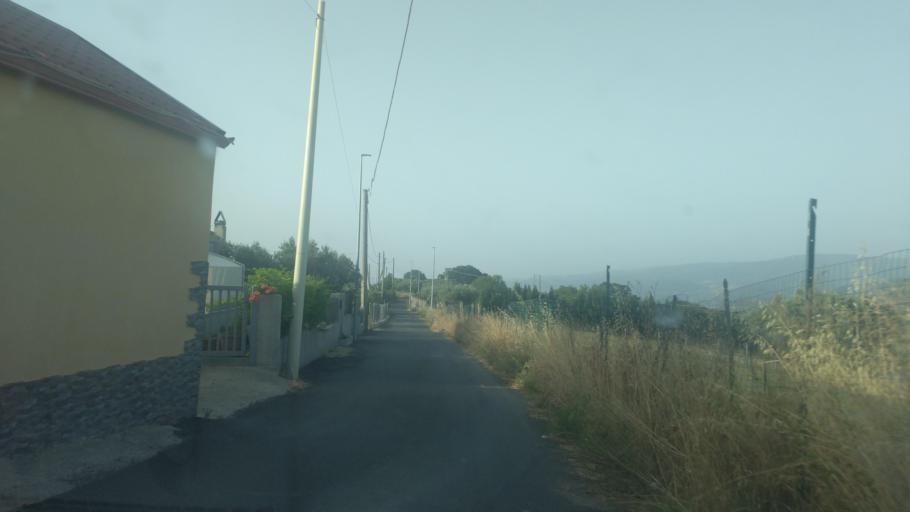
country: IT
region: Calabria
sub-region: Provincia di Catanzaro
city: Staletti
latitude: 38.7627
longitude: 16.5330
